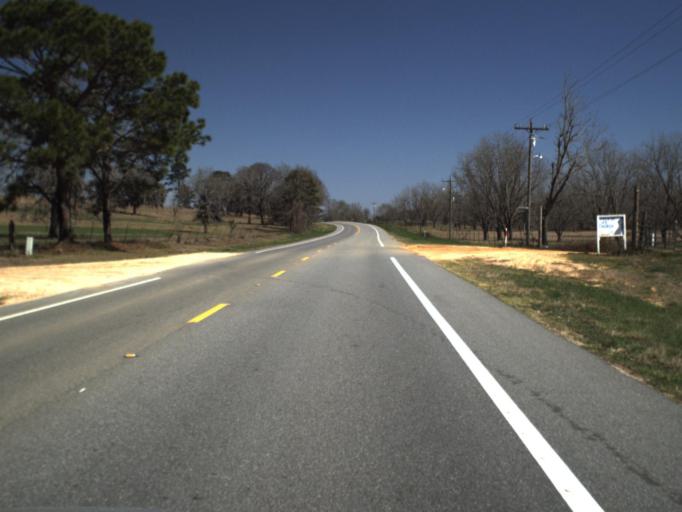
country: US
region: Florida
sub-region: Jackson County
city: Sneads
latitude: 30.6769
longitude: -85.0346
